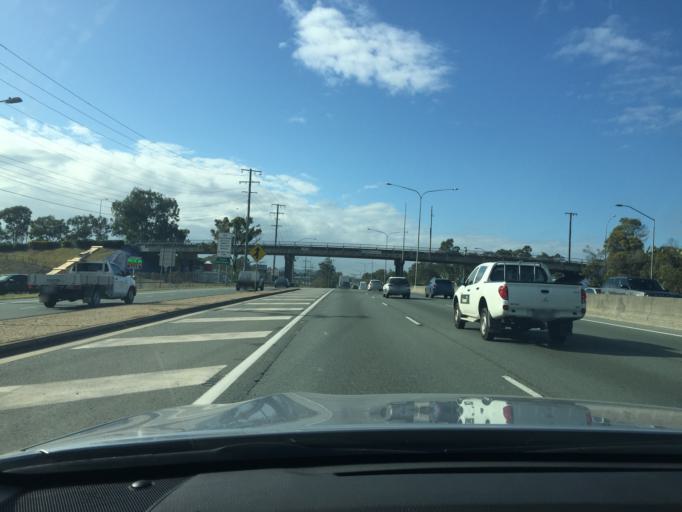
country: AU
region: Queensland
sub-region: Logan
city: Slacks Creek
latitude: -27.6635
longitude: 153.1720
